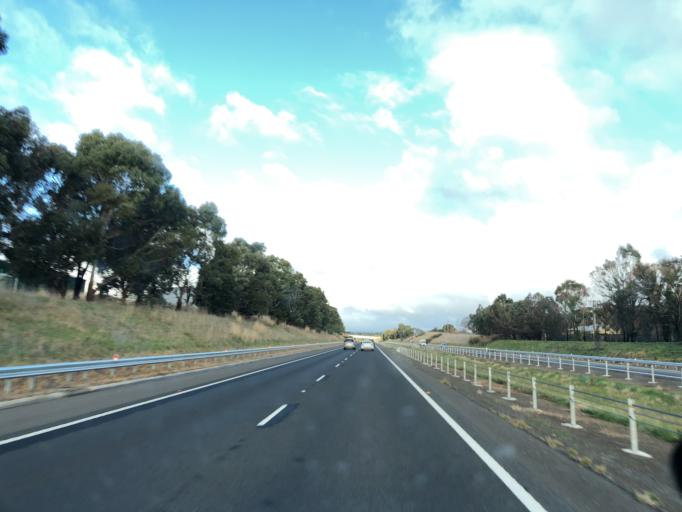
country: AU
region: Victoria
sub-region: Mount Alexander
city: Castlemaine
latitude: -37.2341
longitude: 144.4503
